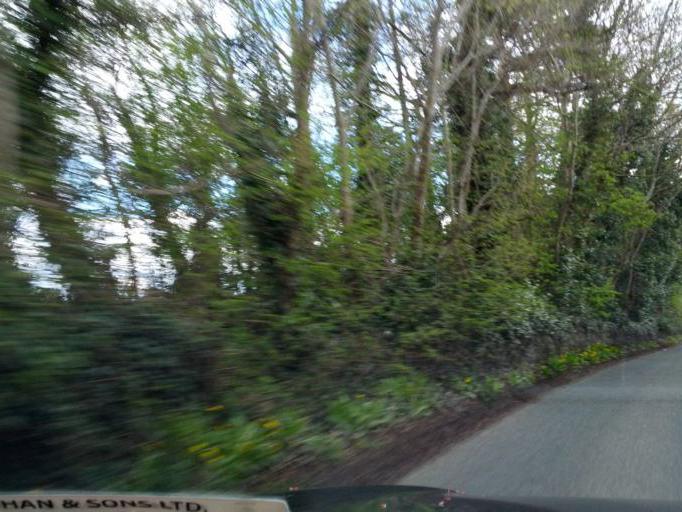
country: IE
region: Leinster
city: Lucan
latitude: 53.3735
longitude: -6.4661
